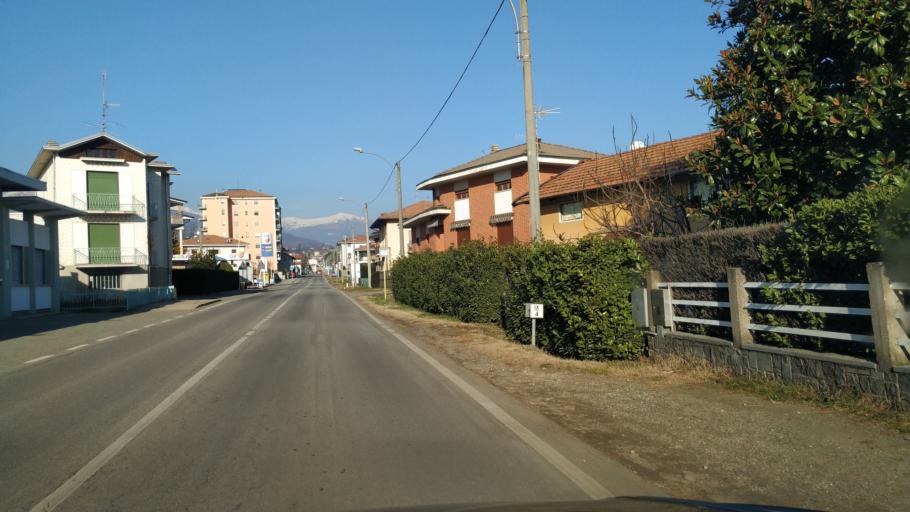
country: IT
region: Piedmont
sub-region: Provincia di Biella
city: Occhieppo Inferiore
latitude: 45.5426
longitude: 8.0133
